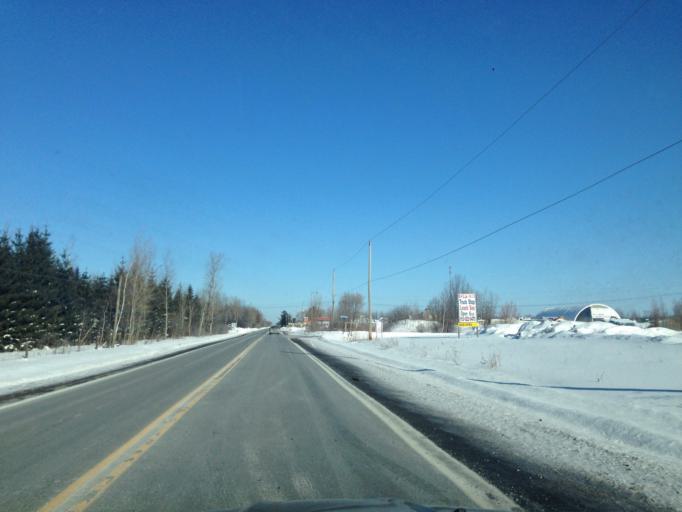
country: CA
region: Ontario
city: Clarence-Rockland
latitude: 45.3373
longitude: -75.4391
